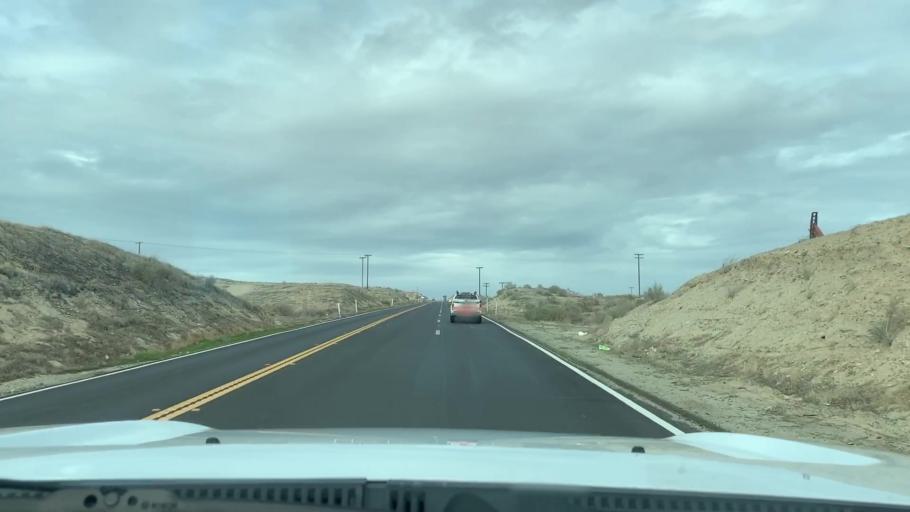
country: US
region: California
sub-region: Kern County
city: South Taft
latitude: 35.1138
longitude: -119.4281
